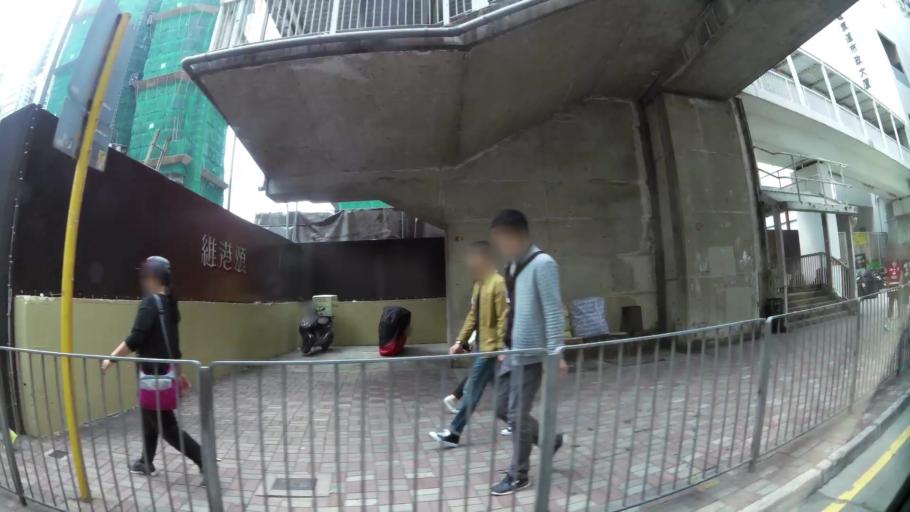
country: HK
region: Wanchai
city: Wan Chai
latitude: 22.2901
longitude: 114.1935
